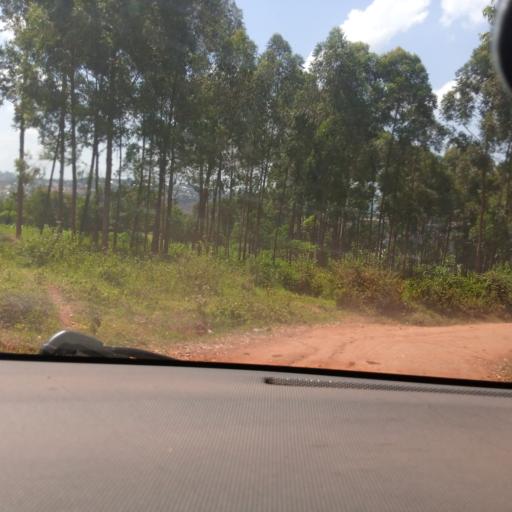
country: UG
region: Central Region
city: Masaka
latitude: -0.3227
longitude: 31.7437
